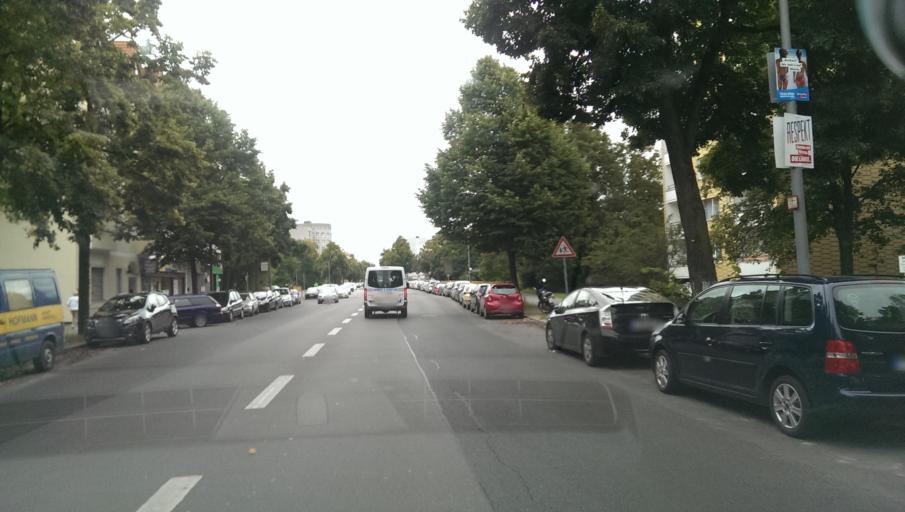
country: DE
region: Berlin
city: Britz
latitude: 52.4593
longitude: 13.4357
